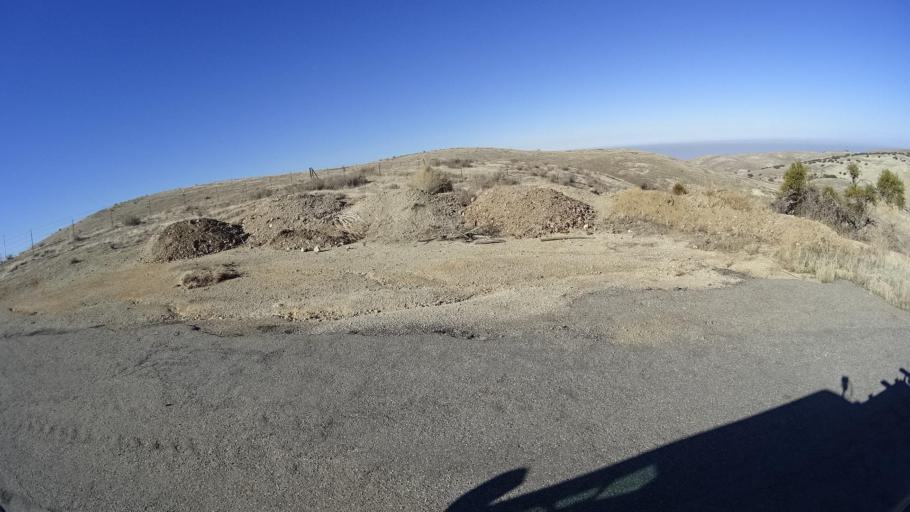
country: US
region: California
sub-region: Kern County
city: Maricopa
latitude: 34.9424
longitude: -119.4046
